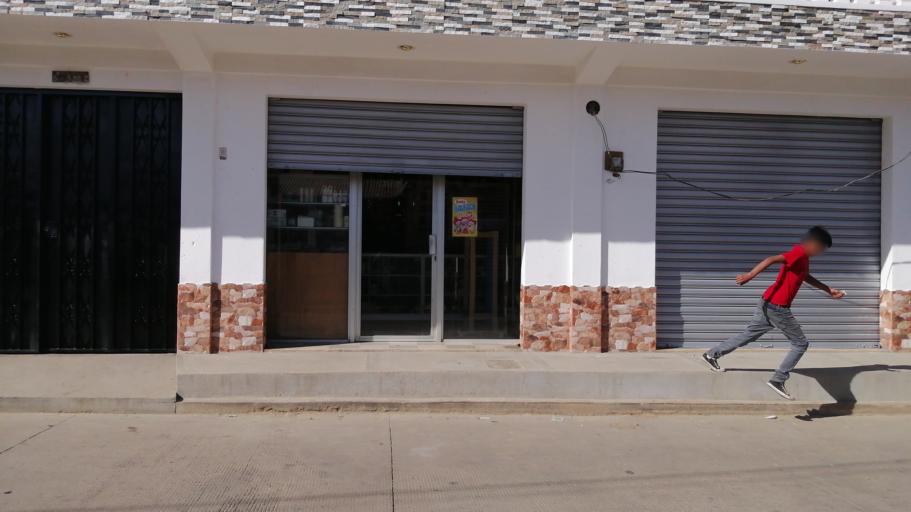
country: GT
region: Quetzaltenango
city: Ostuncalco
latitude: 14.8707
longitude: -91.6257
